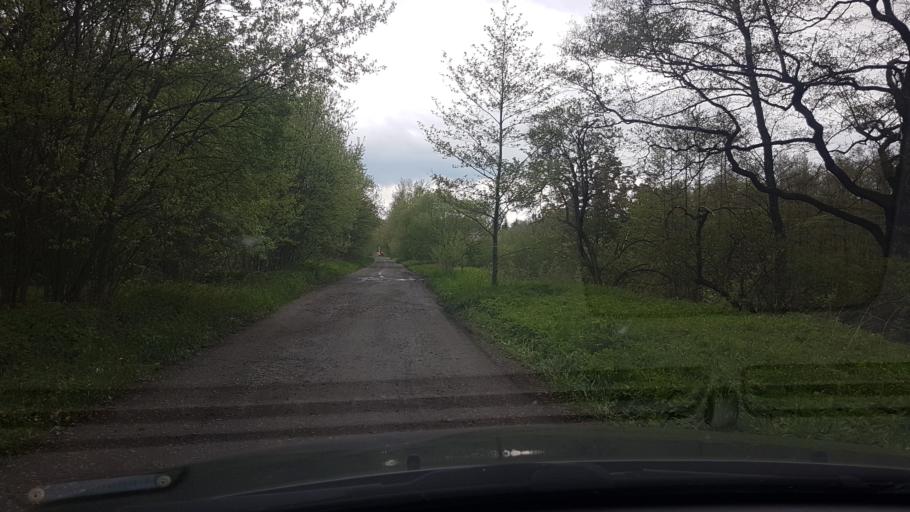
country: CZ
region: Karlovarsky
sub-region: Okres Cheb
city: Cheb
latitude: 50.0567
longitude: 12.3859
